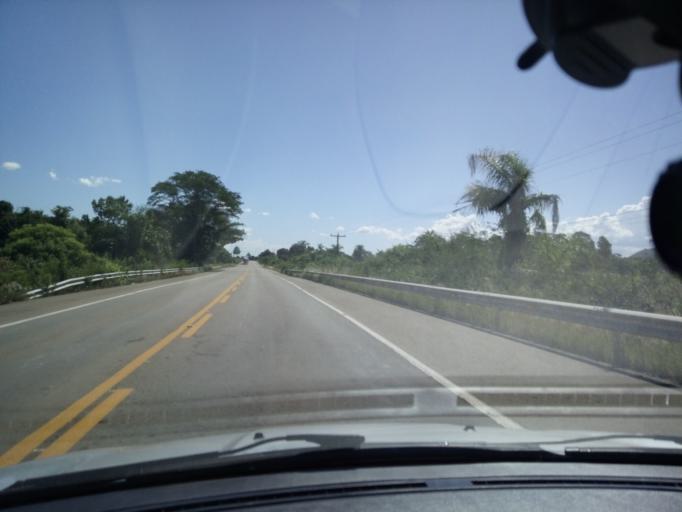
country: BR
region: Rio Grande do Sul
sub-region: Santa Maria
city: Santa Maria
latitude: -29.7324
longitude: -53.5176
